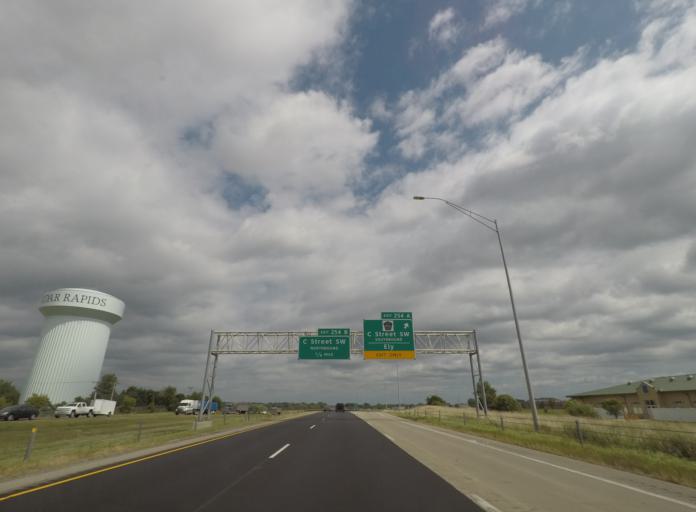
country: US
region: Iowa
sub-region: Linn County
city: Ely
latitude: 41.9267
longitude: -91.6457
